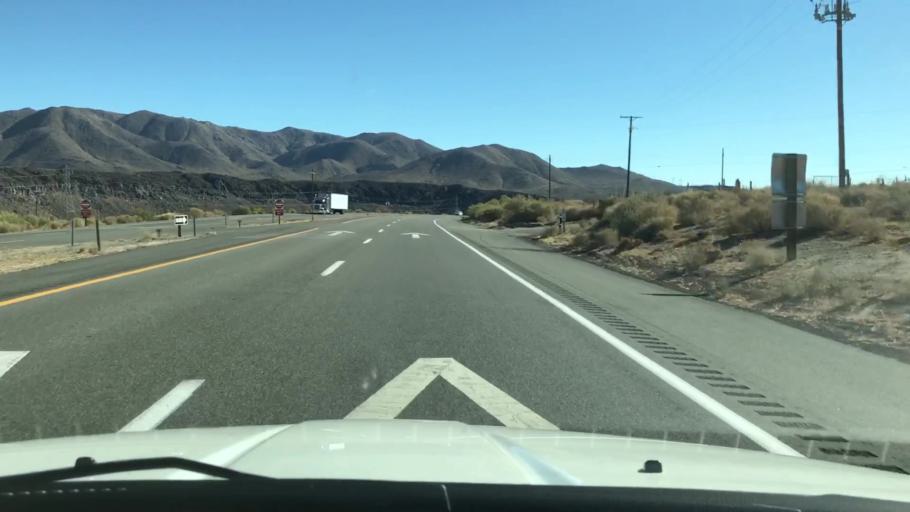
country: US
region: California
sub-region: Kern County
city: Inyokern
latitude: 35.9587
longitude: -117.9127
